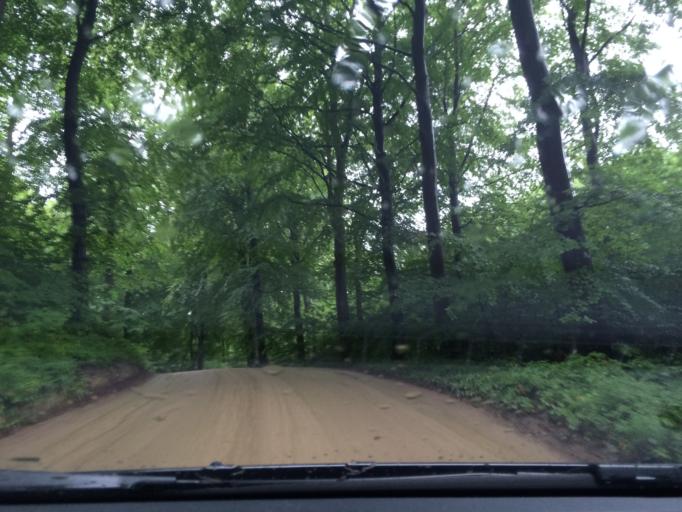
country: DK
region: Zealand
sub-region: Vordingborg Kommune
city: Stege
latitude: 54.9666
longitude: 12.5420
